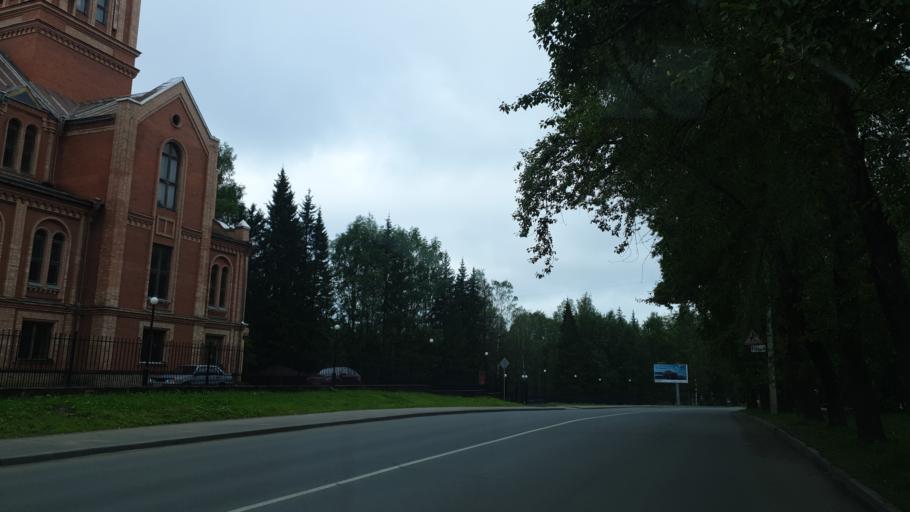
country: RU
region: Komi Republic
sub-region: Syktyvdinskiy Rayon
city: Syktyvkar
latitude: 61.6597
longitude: 50.8226
